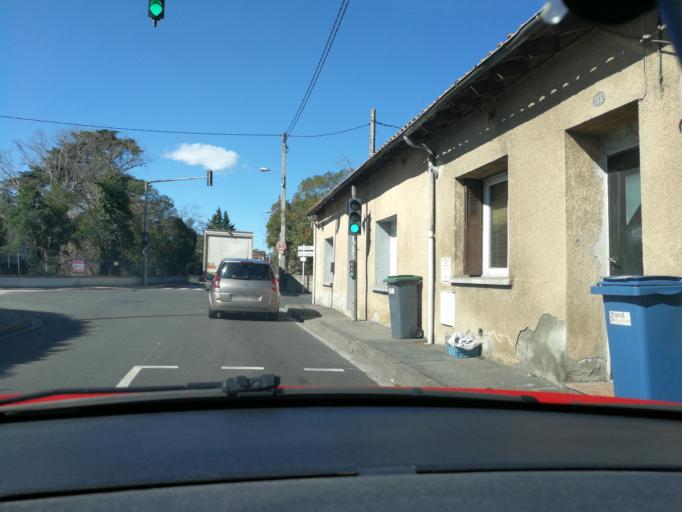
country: FR
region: Midi-Pyrenees
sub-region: Departement de la Haute-Garonne
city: Cugnaux
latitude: 43.5532
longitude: 1.3755
